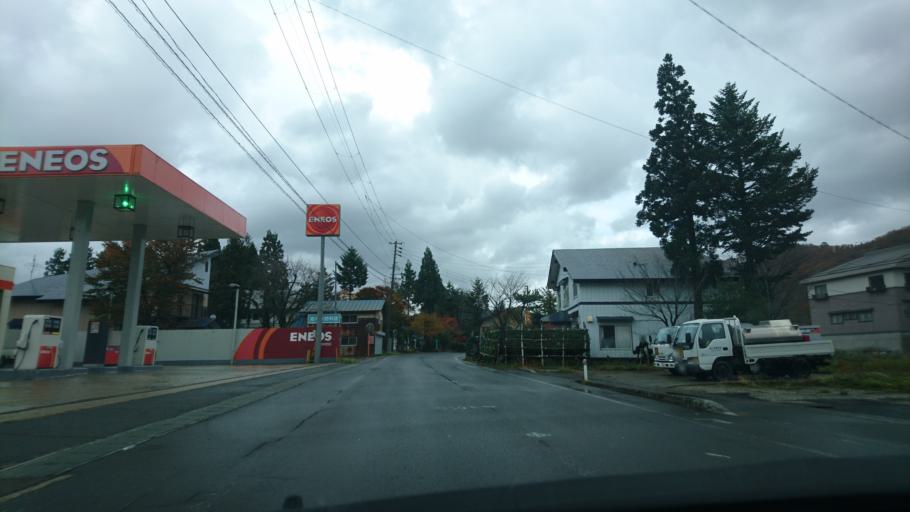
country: JP
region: Akita
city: Kakunodatemachi
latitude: 39.4811
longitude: 140.7987
